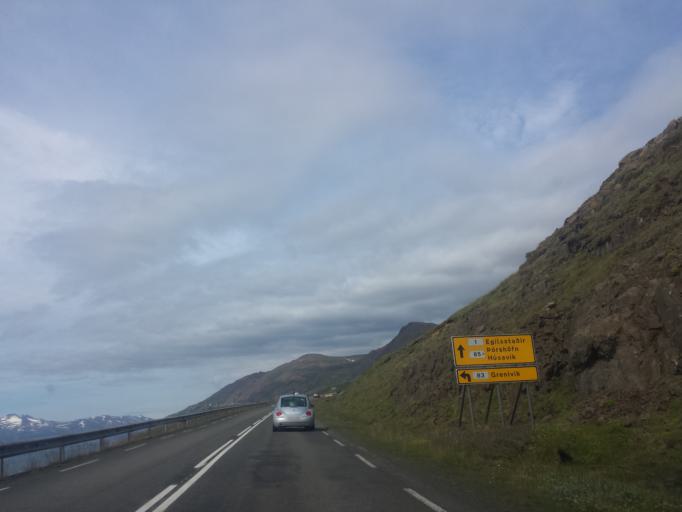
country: IS
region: Northeast
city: Akureyri
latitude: 65.7971
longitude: -18.0583
